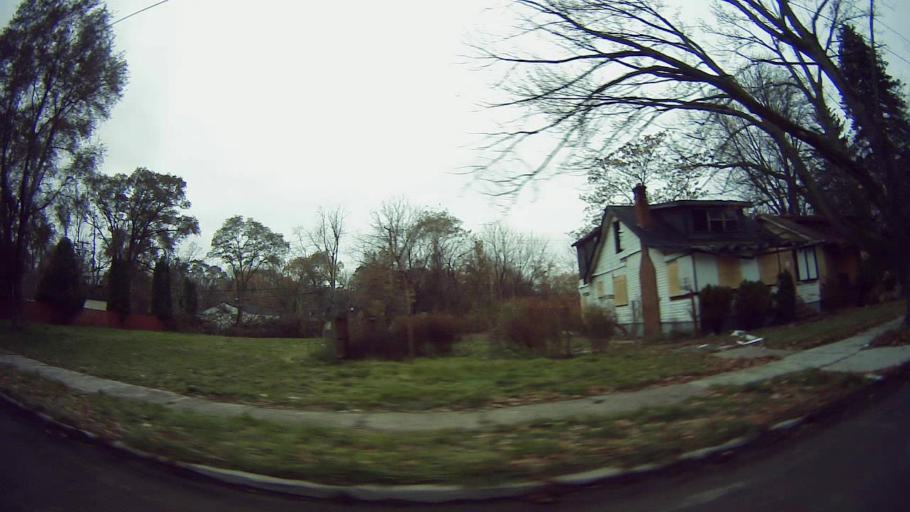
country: US
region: Michigan
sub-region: Oakland County
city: Southfield
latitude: 42.4233
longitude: -83.2386
